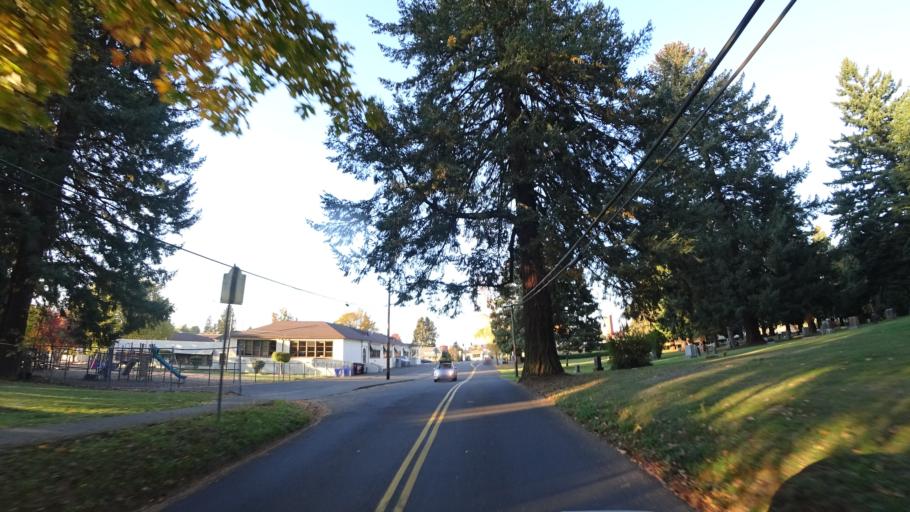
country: US
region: Oregon
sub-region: Multnomah County
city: Gresham
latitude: 45.4959
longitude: -122.4346
